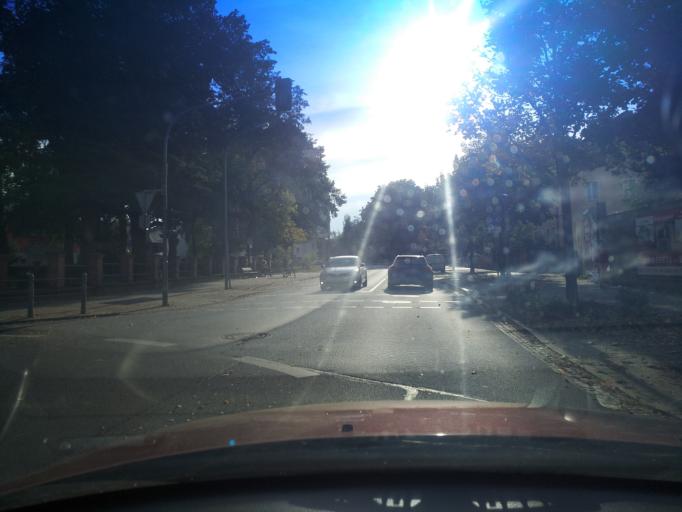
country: DE
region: Saxony
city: Bautzen
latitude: 51.1839
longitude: 14.4352
